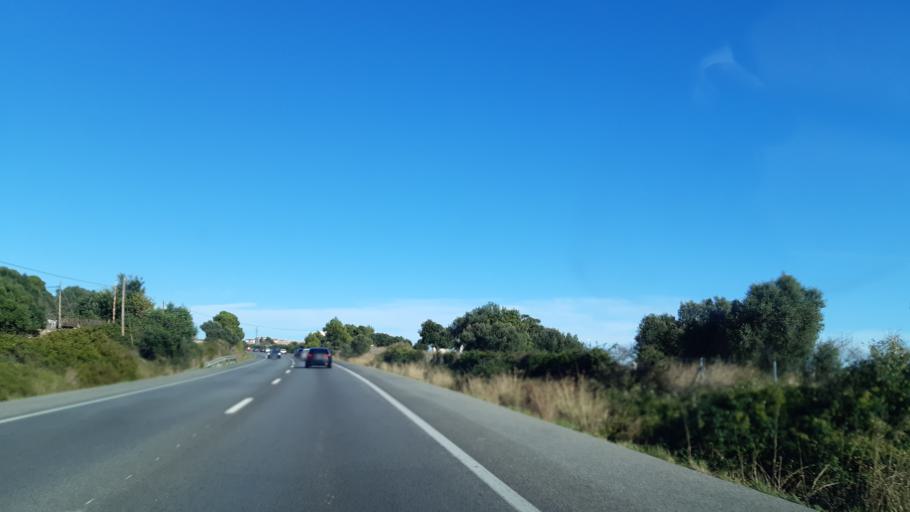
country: ES
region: Catalonia
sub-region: Provincia de Barcelona
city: Vilanova i la Geltru
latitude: 41.2175
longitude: 1.6985
